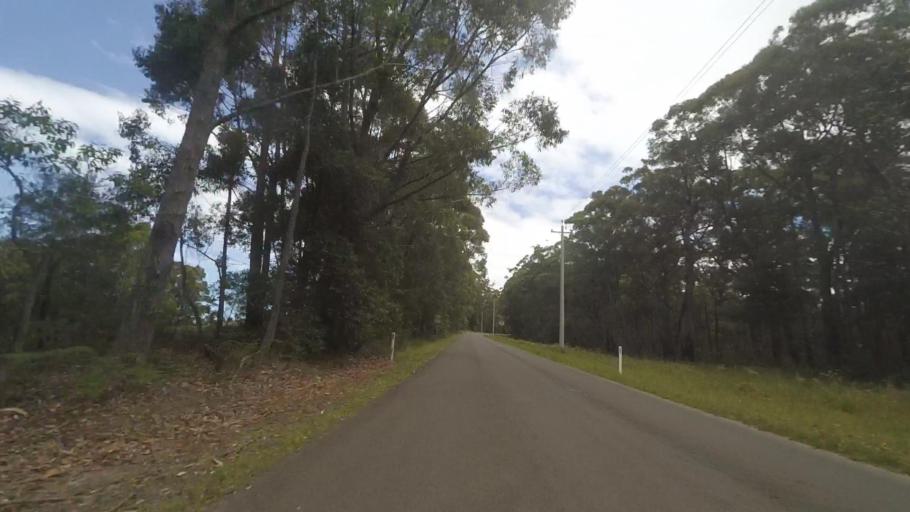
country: AU
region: New South Wales
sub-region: Shoalhaven Shire
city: Milton
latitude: -35.3803
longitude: 150.3728
